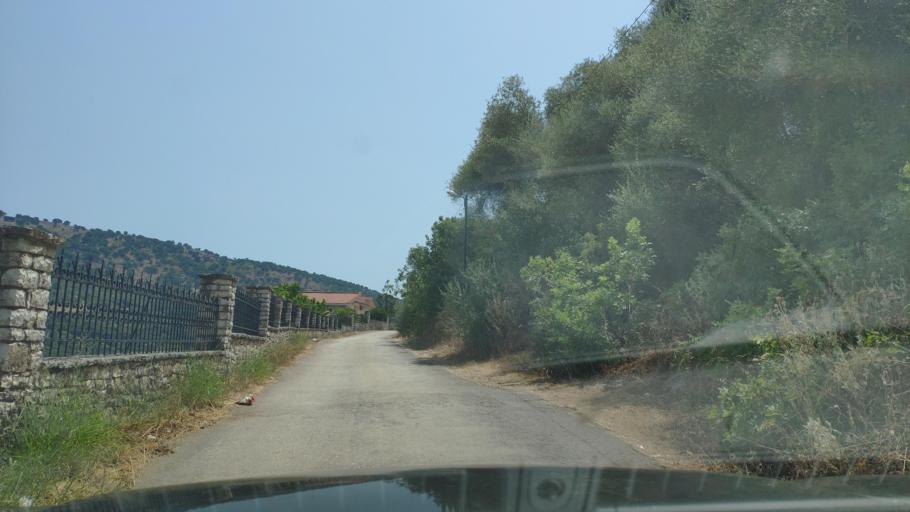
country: GR
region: West Greece
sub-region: Nomos Aitolias kai Akarnanias
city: Amfilochia
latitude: 38.8683
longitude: 21.0739
